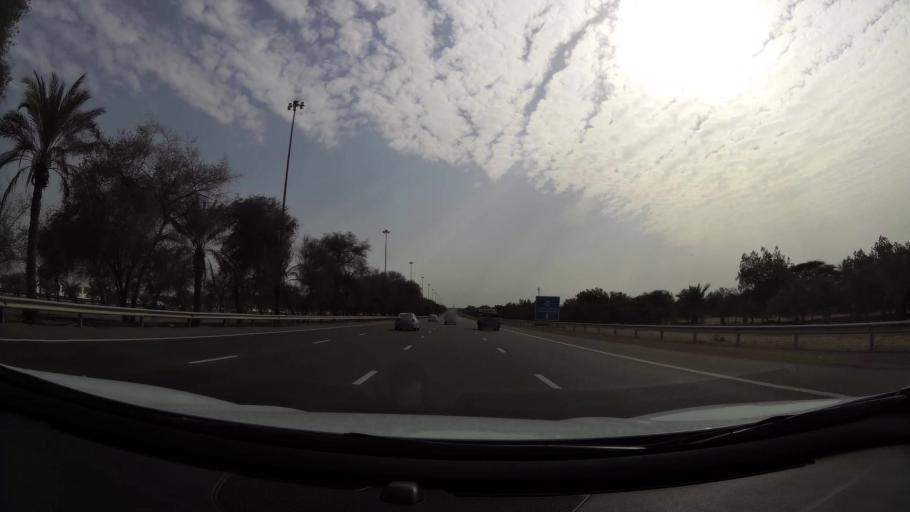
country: AE
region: Abu Dhabi
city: Abu Dhabi
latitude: 24.4980
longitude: 54.6803
